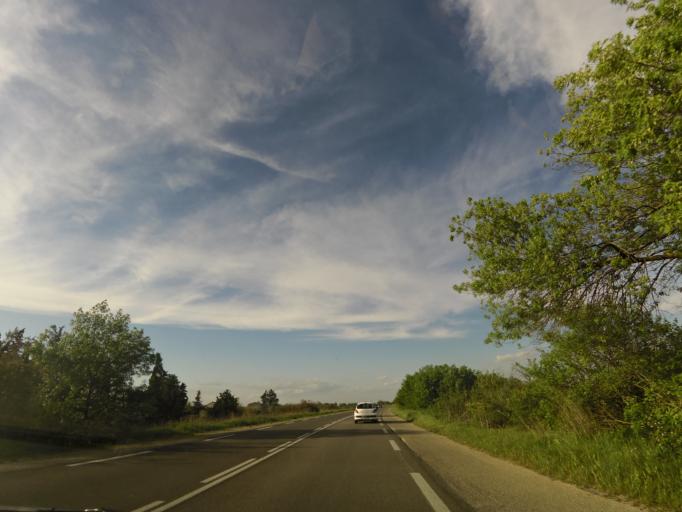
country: FR
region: Languedoc-Roussillon
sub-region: Departement de l'Herault
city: La Grande-Motte
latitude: 43.5989
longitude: 4.1054
